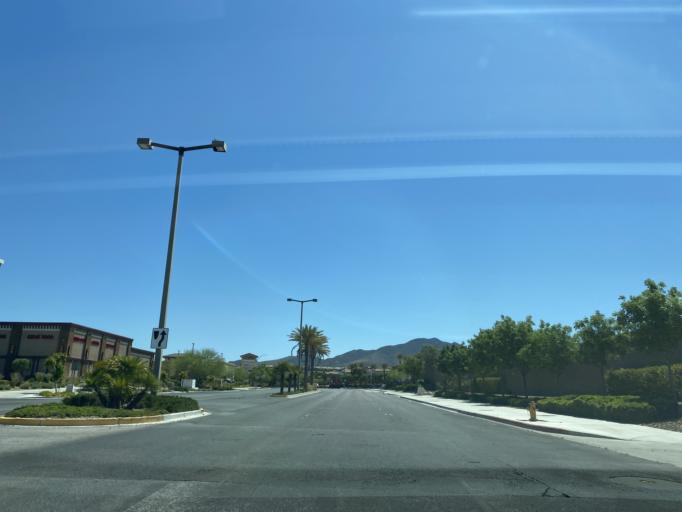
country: US
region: Nevada
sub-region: Clark County
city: Whitney
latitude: 35.9410
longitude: -115.1192
